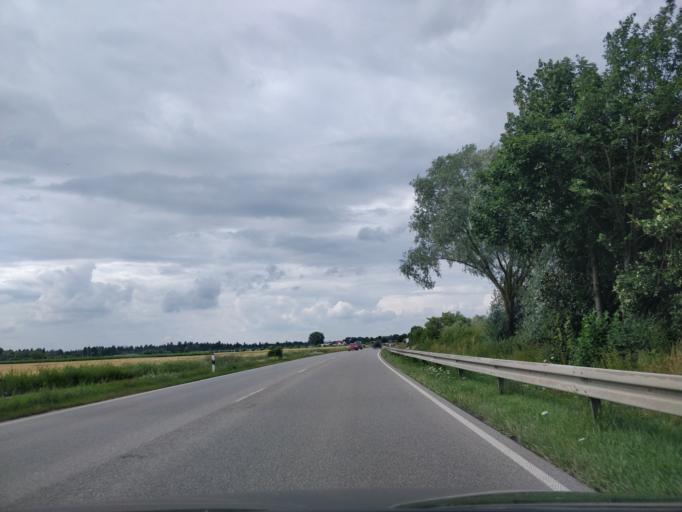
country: DE
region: Bavaria
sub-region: Swabia
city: Kissing
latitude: 48.2856
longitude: 10.9686
